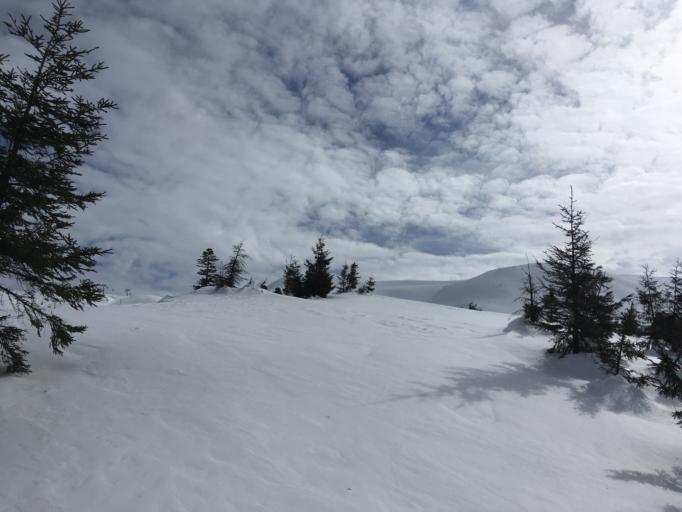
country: GE
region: Ajaria
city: Dioknisi
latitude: 41.6223
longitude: 42.4950
